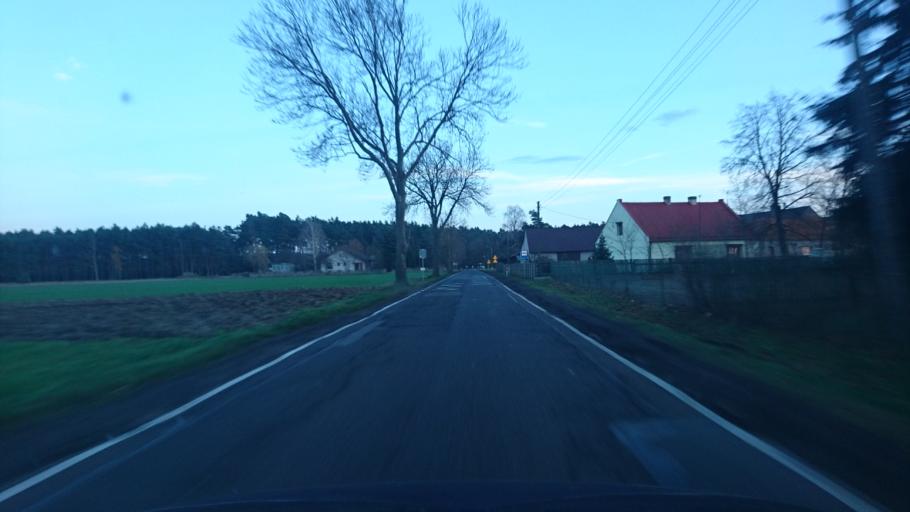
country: PL
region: Greater Poland Voivodeship
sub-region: Powiat ostrowski
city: Odolanow
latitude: 51.5400
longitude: 17.7185
